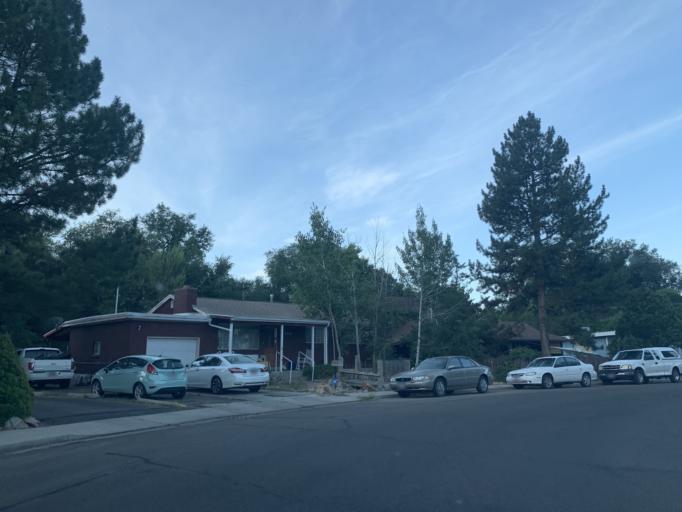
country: US
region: Utah
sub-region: Utah County
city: Provo
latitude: 40.2478
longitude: -111.6721
